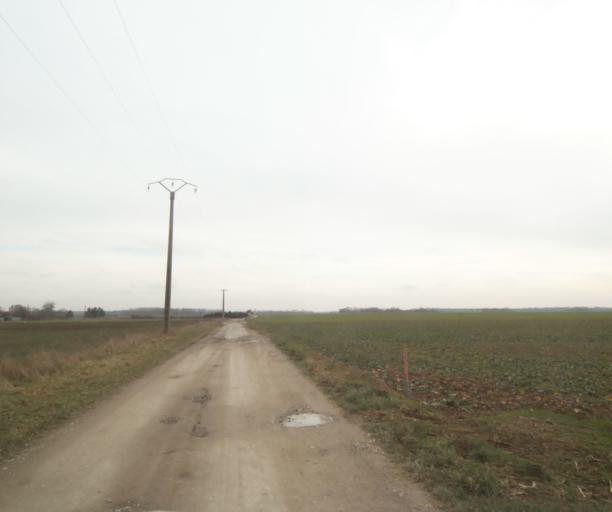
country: FR
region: Champagne-Ardenne
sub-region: Departement de la Haute-Marne
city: Villiers-en-Lieu
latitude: 48.6751
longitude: 4.8704
